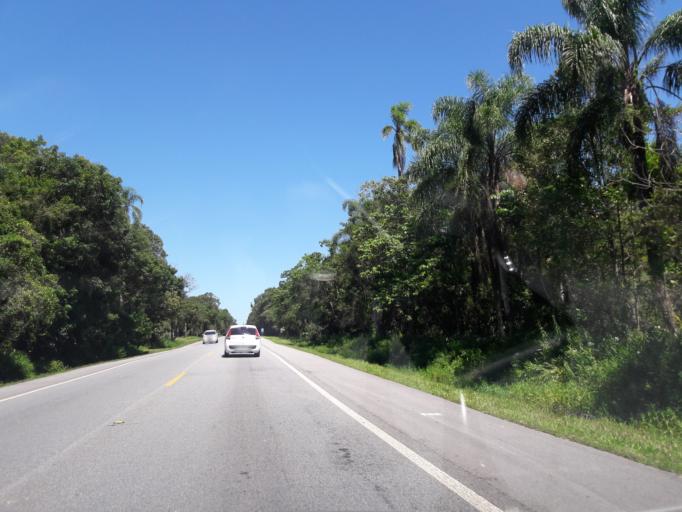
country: BR
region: Parana
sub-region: Pontal Do Parana
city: Pontal do Parana
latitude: -25.6536
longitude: -48.5254
